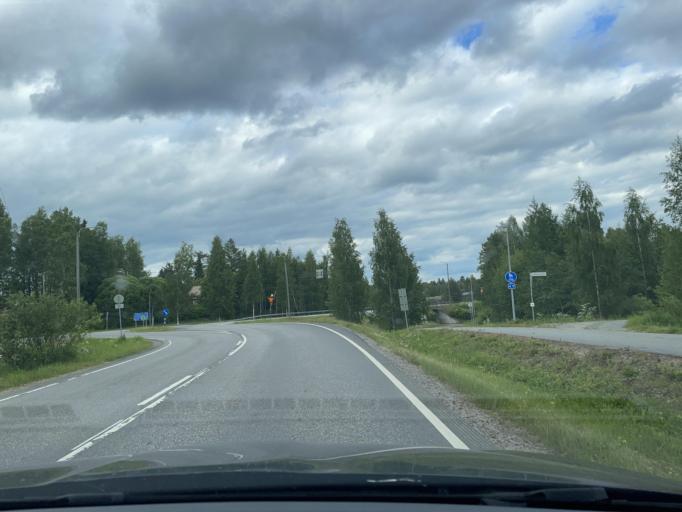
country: FI
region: Central Finland
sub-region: Jyvaeskylae
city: Petaejaevesi
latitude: 62.2468
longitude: 25.1709
